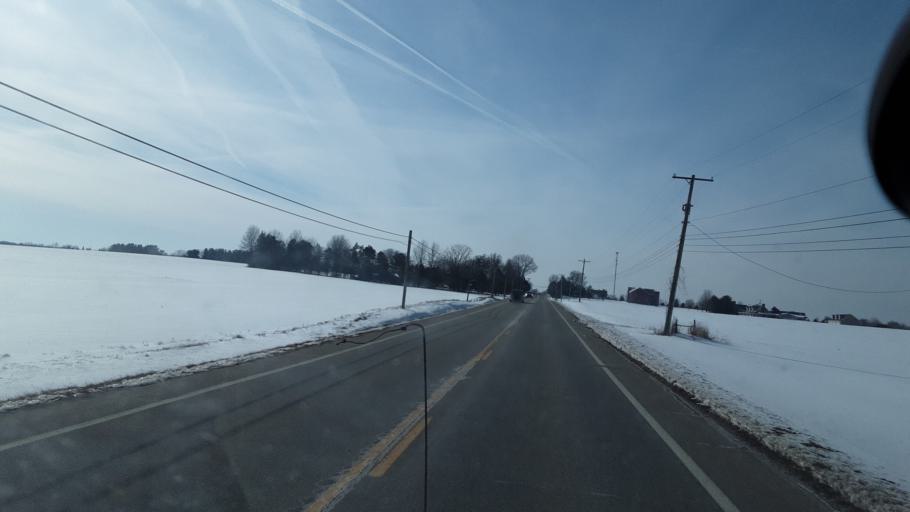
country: US
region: Ohio
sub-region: Mahoning County
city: Craig Beach
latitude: 41.0241
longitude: -80.8942
